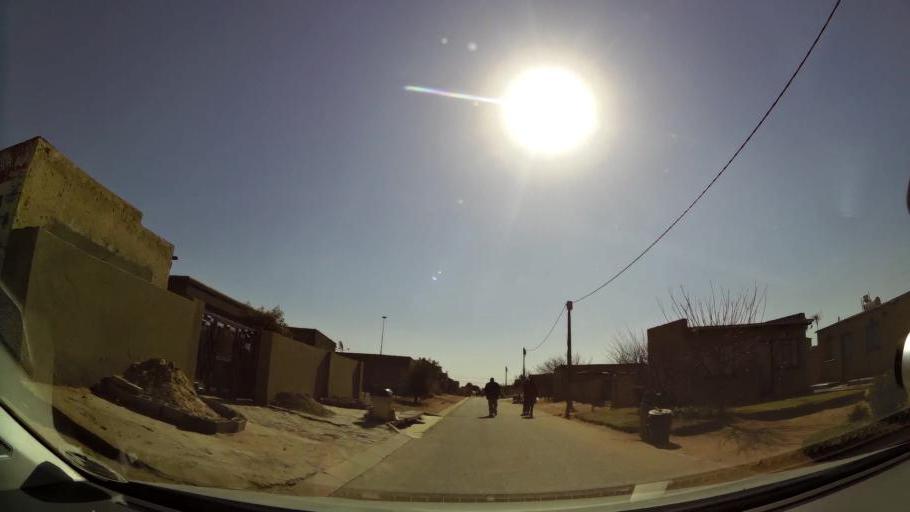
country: ZA
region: Gauteng
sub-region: Ekurhuleni Metropolitan Municipality
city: Tembisa
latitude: -26.0267
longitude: 28.2377
